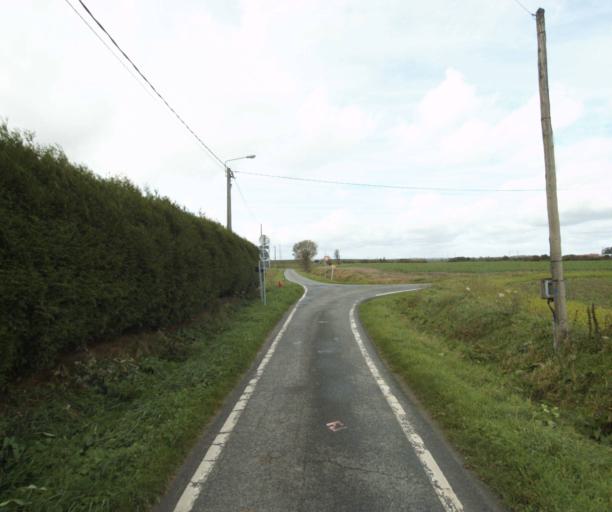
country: FR
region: Nord-Pas-de-Calais
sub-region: Departement du Nord
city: Houplines
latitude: 50.6719
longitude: 2.9239
